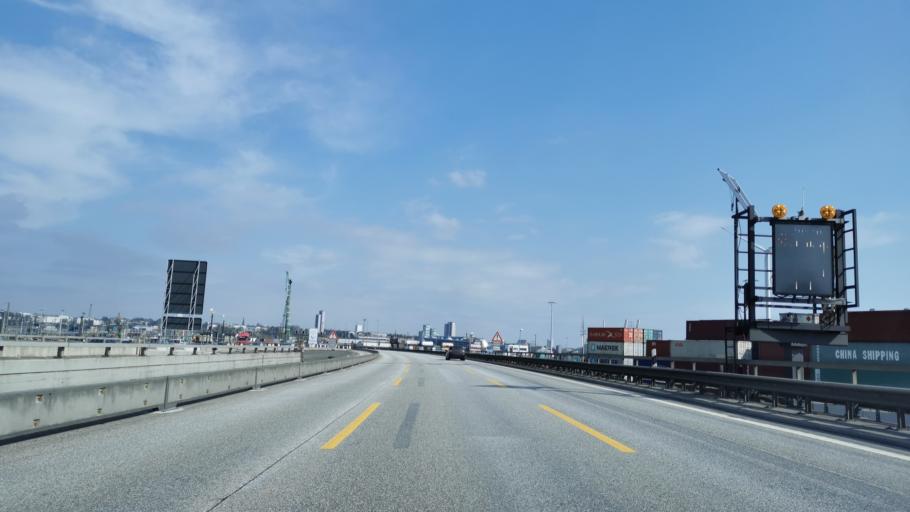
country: DE
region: Hamburg
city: Altona
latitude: 53.5246
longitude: 9.9276
